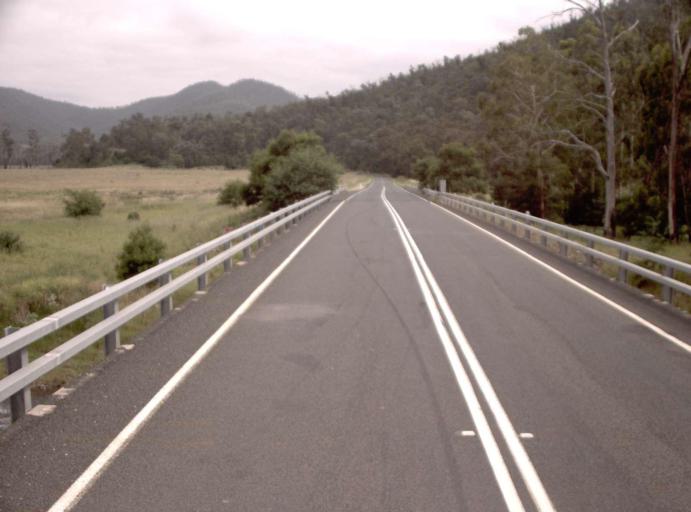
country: AU
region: Victoria
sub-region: Wellington
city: Heyfield
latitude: -37.7622
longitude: 146.6688
